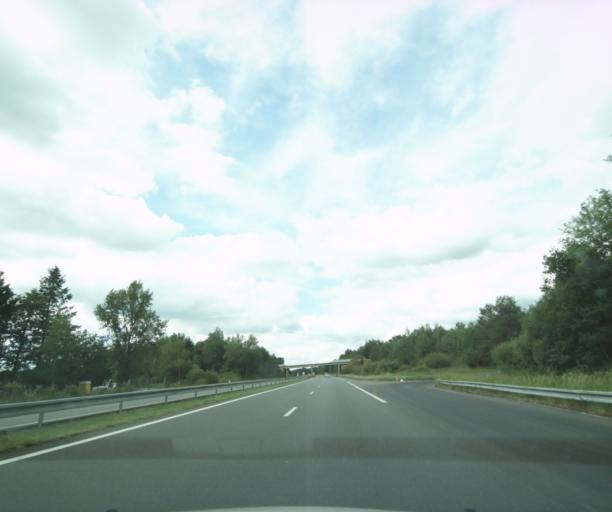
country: FR
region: Centre
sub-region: Departement du Loir-et-Cher
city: Nouan-le-Fuzelier
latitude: 47.4759
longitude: 2.0091
